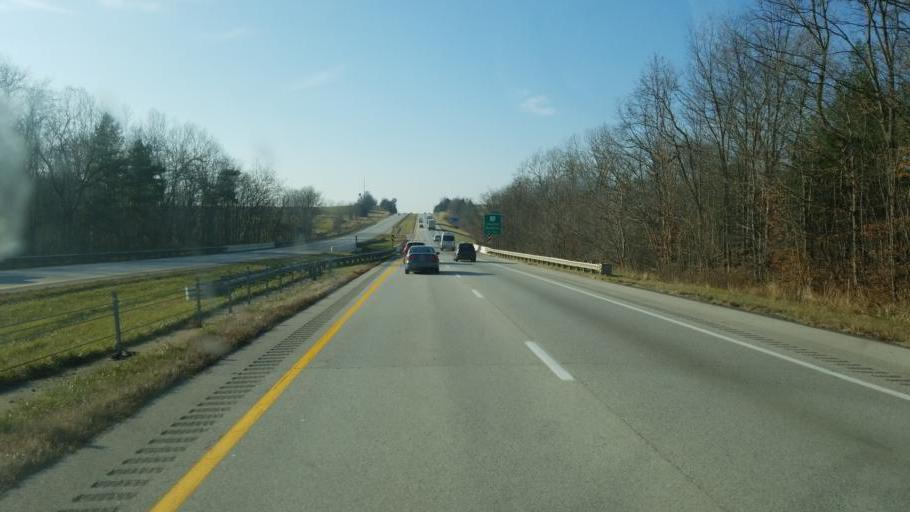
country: US
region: Ohio
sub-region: Medina County
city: Seville
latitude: 41.0329
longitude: -81.8502
